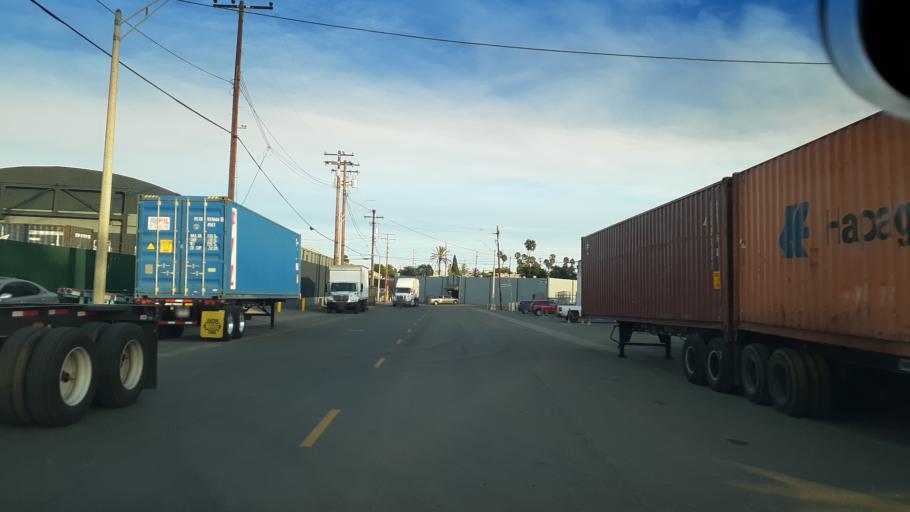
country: US
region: California
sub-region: Los Angeles County
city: Long Beach
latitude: 33.7817
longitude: -118.2026
